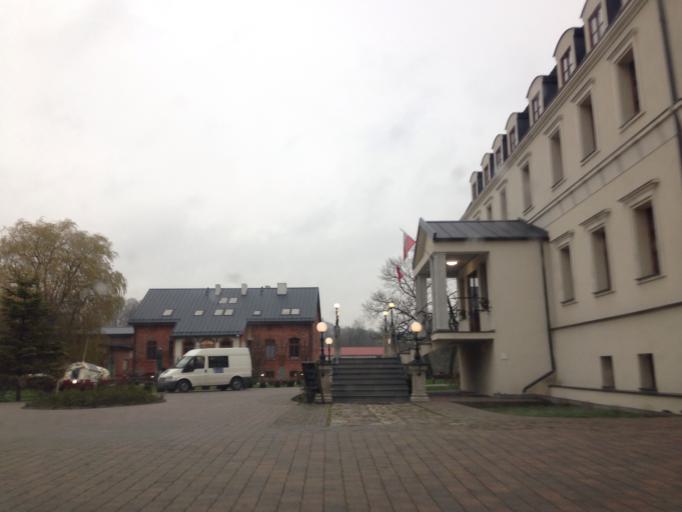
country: PL
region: Pomeranian Voivodeship
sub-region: Powiat gdanski
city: Przywidz
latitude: 54.1956
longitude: 18.3227
